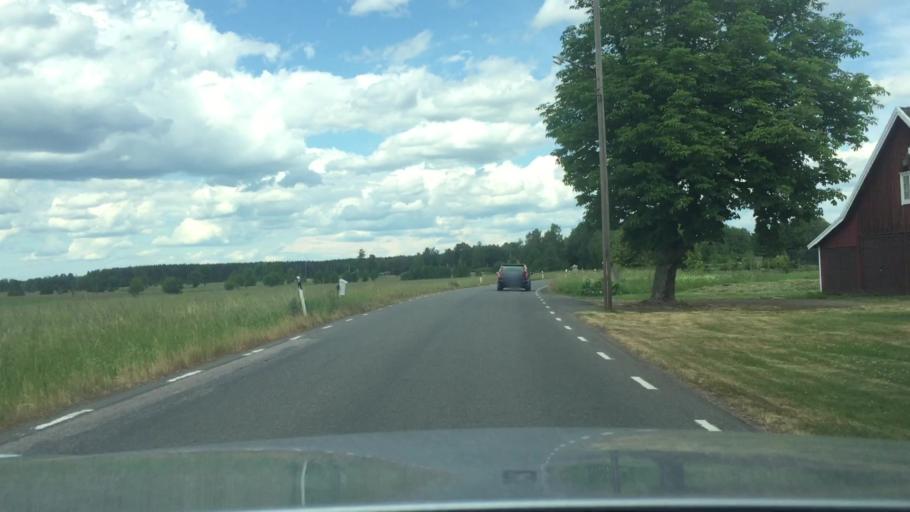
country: SE
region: Vaestra Goetaland
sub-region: Tidaholms Kommun
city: Tidaholm
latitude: 58.1919
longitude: 13.9764
